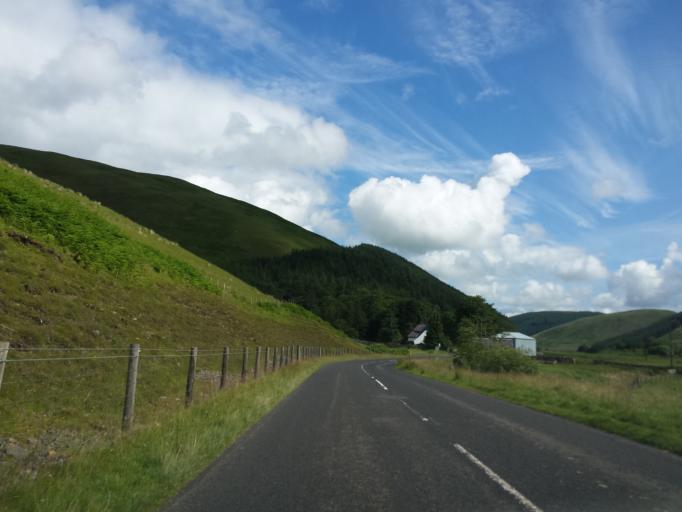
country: GB
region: Scotland
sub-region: The Scottish Borders
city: Peebles
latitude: 55.4562
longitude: -3.2198
